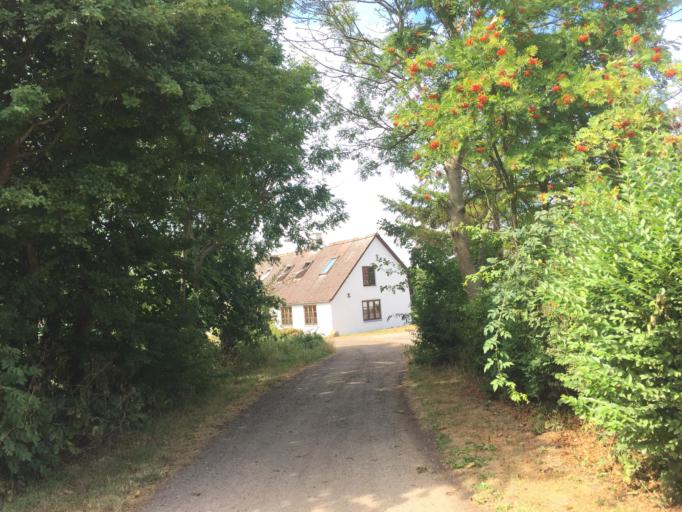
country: DK
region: Central Jutland
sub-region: Samso Kommune
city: Tranebjerg
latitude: 55.9475
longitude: 10.4407
